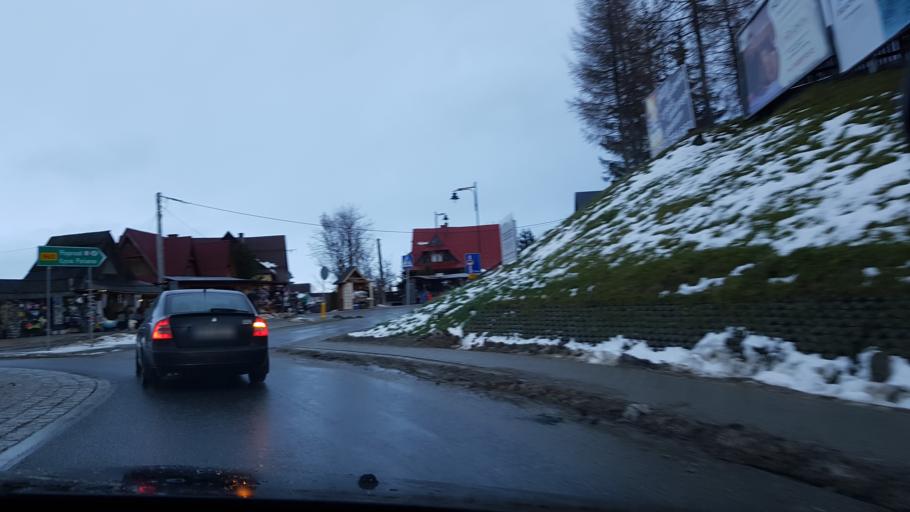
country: PL
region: Lesser Poland Voivodeship
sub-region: Powiat tatrzanski
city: Bukowina Tatrzanska
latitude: 49.3297
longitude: 20.0972
